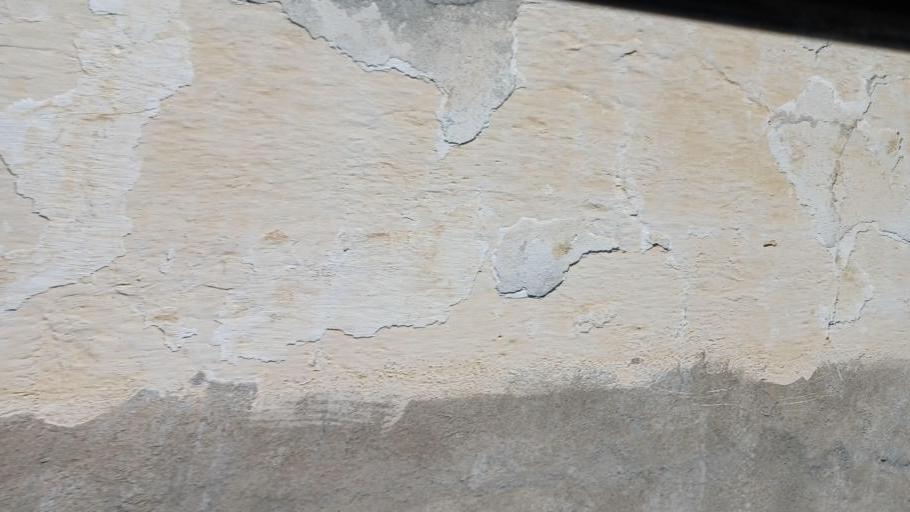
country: CY
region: Lefkosia
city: Kakopetria
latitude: 35.0393
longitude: 32.9012
